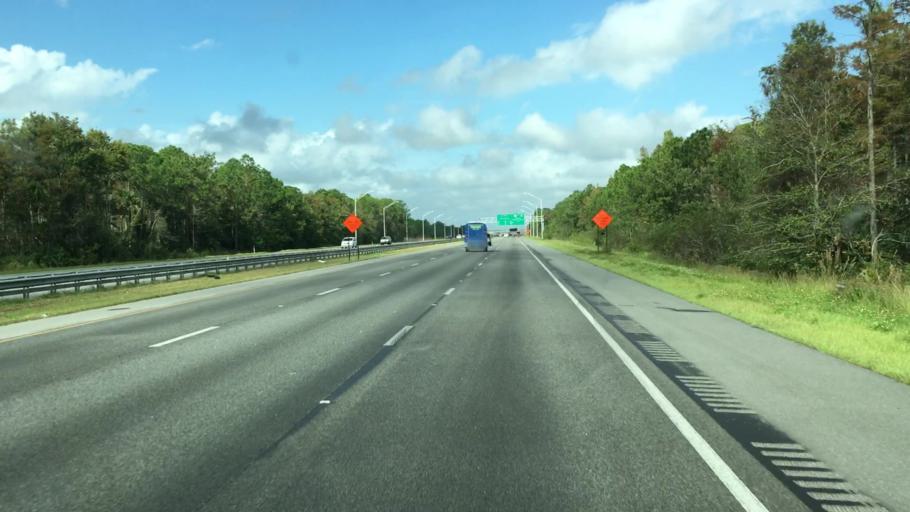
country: US
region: Florida
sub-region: Volusia County
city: South Daytona
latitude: 29.1367
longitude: -81.0647
